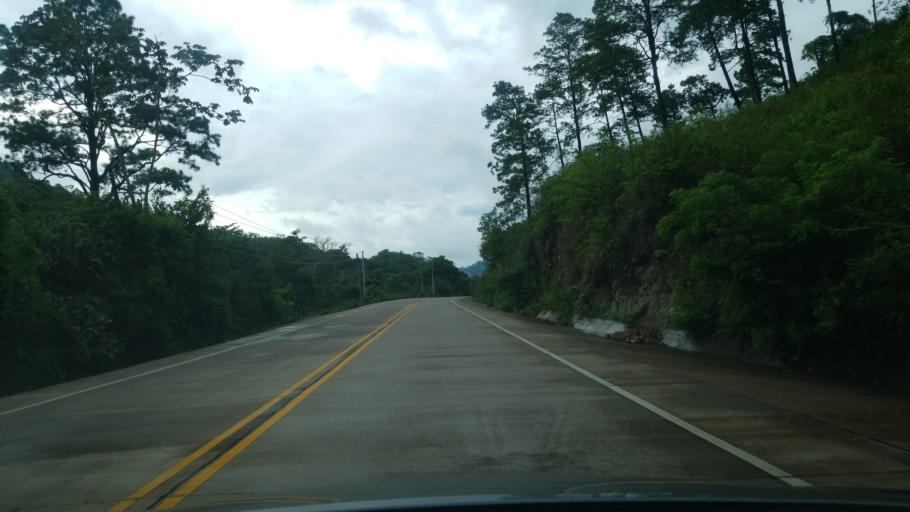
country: HN
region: Copan
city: Copan
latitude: 14.8505
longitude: -89.1977
